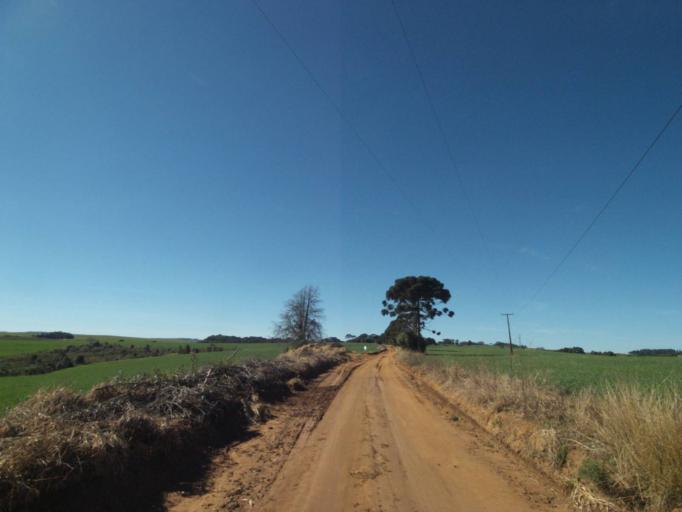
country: BR
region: Parana
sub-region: Tibagi
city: Tibagi
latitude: -24.5925
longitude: -50.2523
